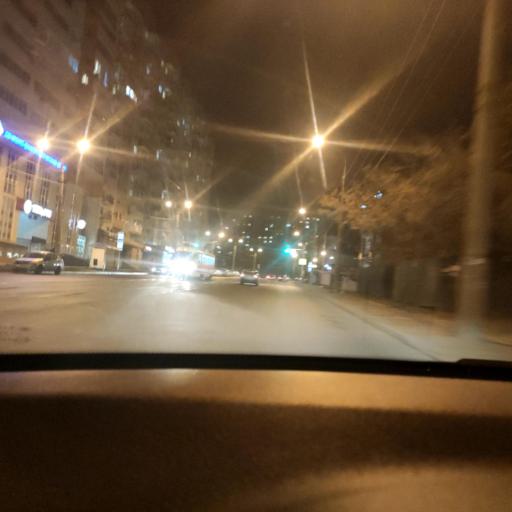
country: RU
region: Samara
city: Samara
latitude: 53.1942
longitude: 50.1513
